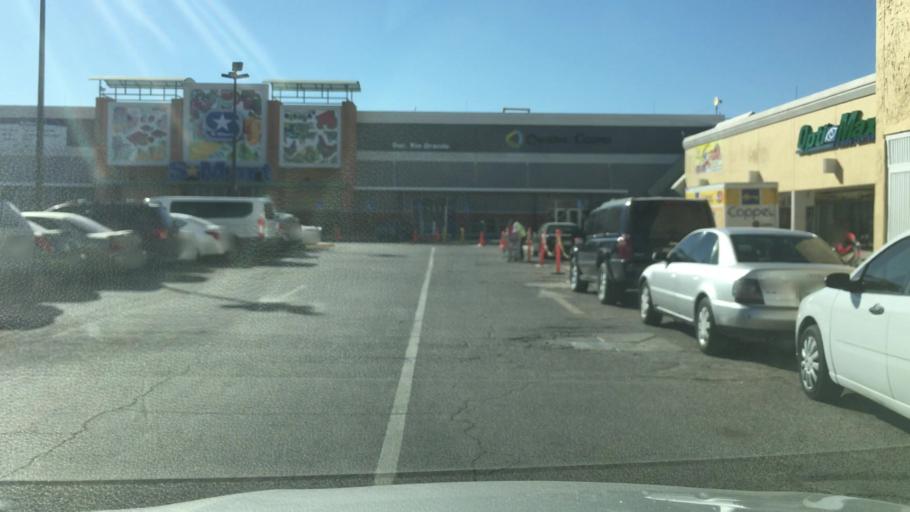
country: MX
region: Chihuahua
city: Ciudad Juarez
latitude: 31.7358
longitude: -106.4462
